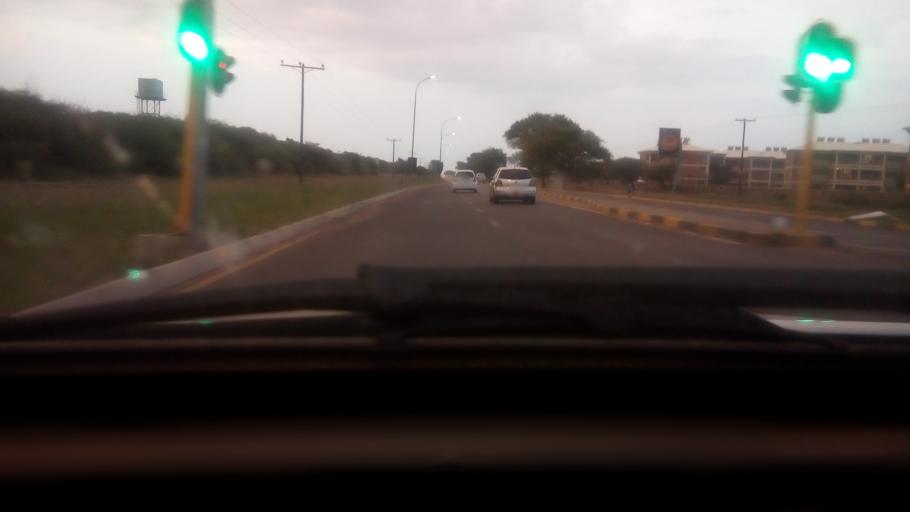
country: BW
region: South East
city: Gaborone
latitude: -24.6043
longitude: 25.9228
